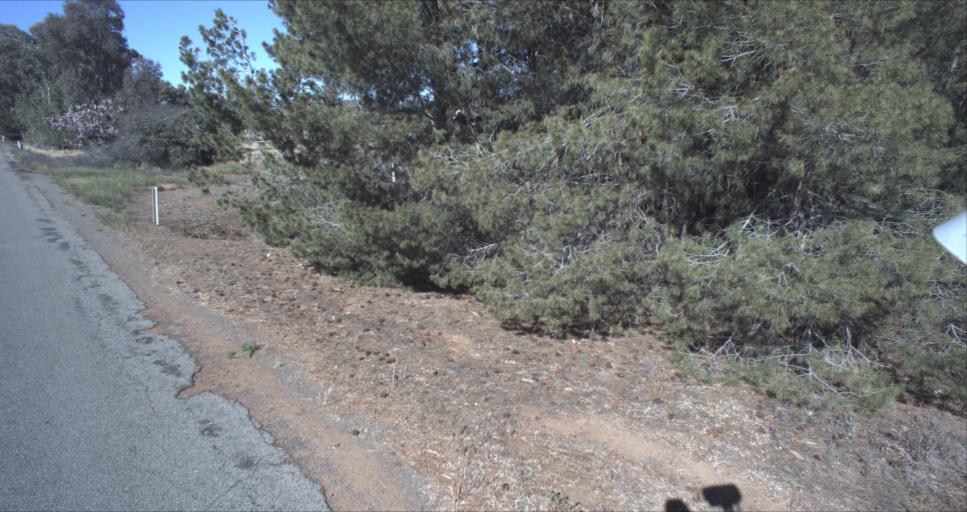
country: AU
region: New South Wales
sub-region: Leeton
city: Leeton
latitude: -34.5724
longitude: 146.3104
